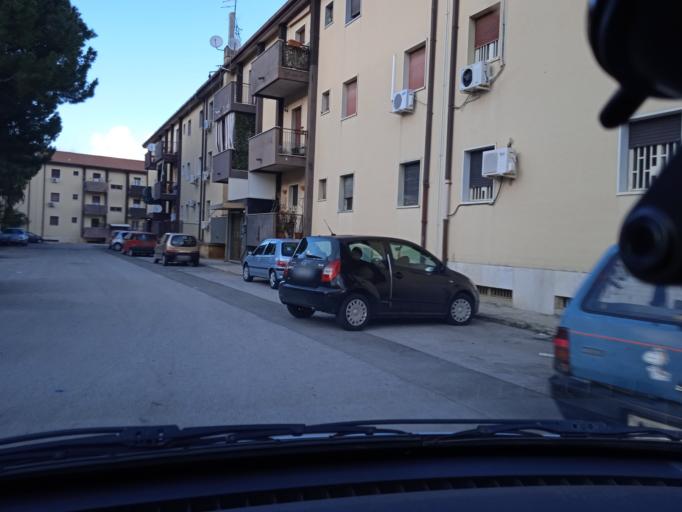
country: IT
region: Sicily
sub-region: Palermo
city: Villa Ciambra
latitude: 38.0849
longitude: 13.3599
